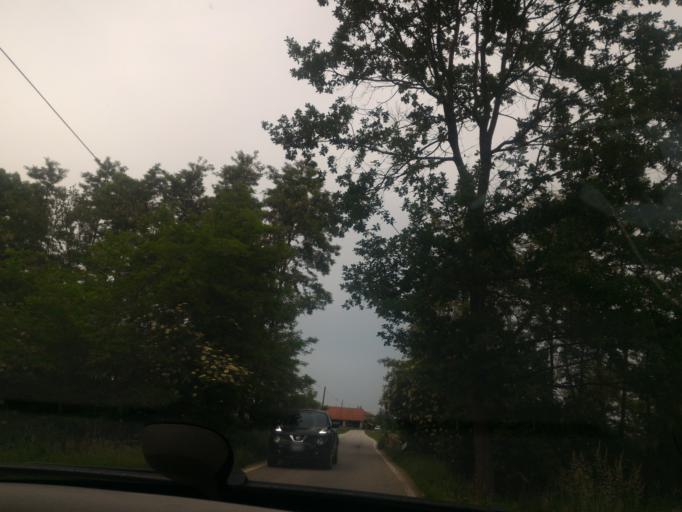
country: IT
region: Piedmont
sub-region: Provincia di Cuneo
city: Beinette
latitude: 44.3653
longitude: 7.6138
